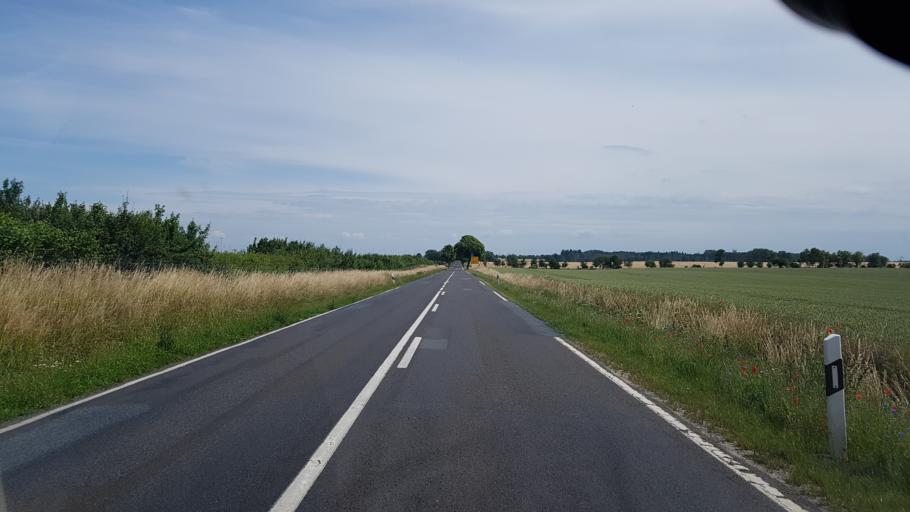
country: DE
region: Mecklenburg-Vorpommern
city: Strasburg
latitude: 53.4021
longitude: 13.7496
